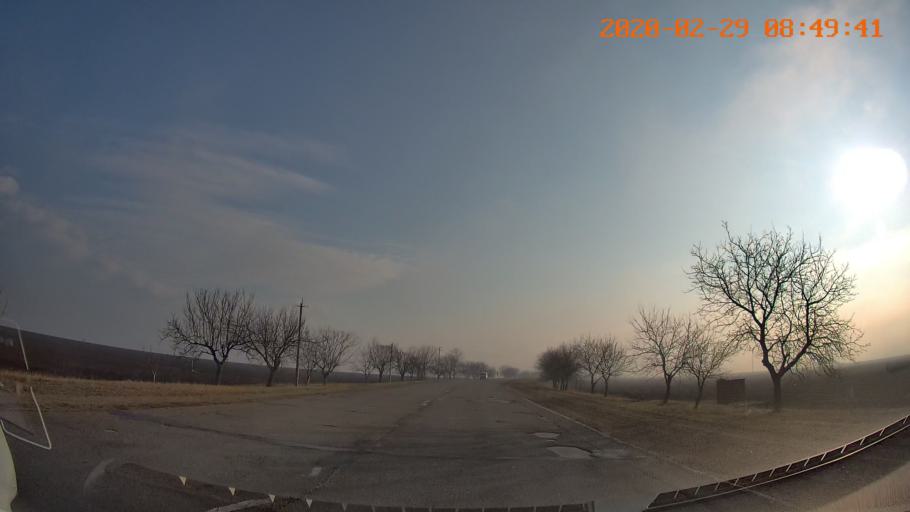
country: MD
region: Anenii Noi
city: Varnita
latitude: 46.9217
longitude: 29.4998
